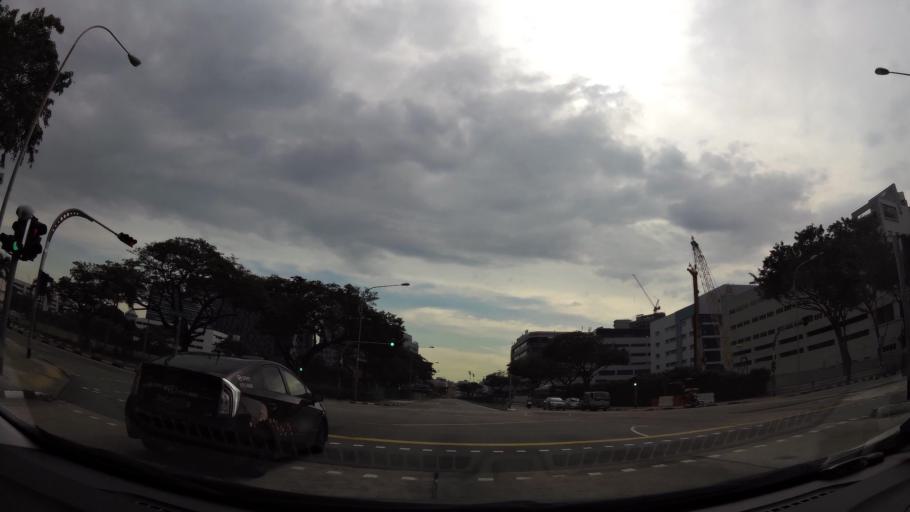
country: SG
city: Singapore
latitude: 1.3155
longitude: 103.8646
